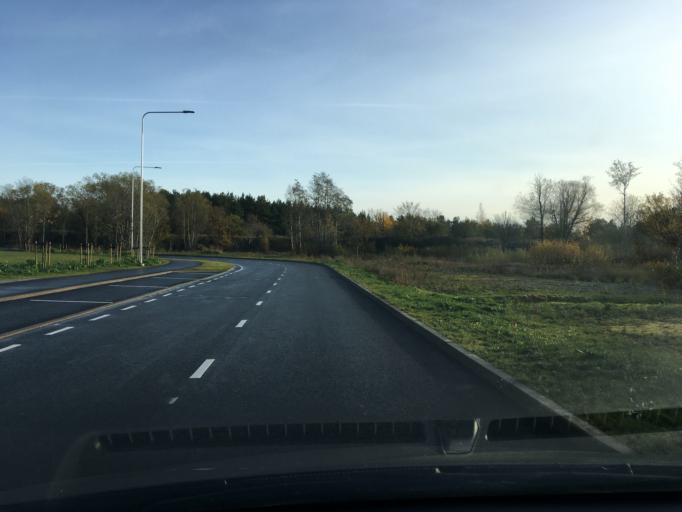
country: EE
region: Harju
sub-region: Viimsi vald
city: Viimsi
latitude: 59.4504
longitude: 24.8176
